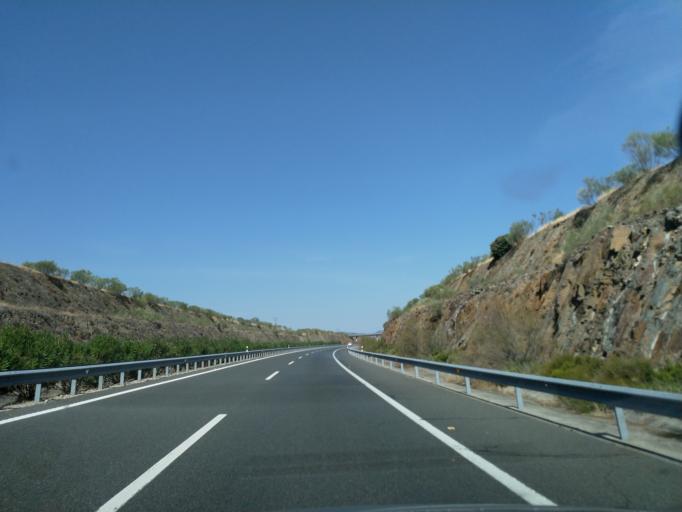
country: ES
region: Extremadura
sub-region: Provincia de Caceres
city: Aldea del Cano
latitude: 39.3414
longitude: -6.3406
